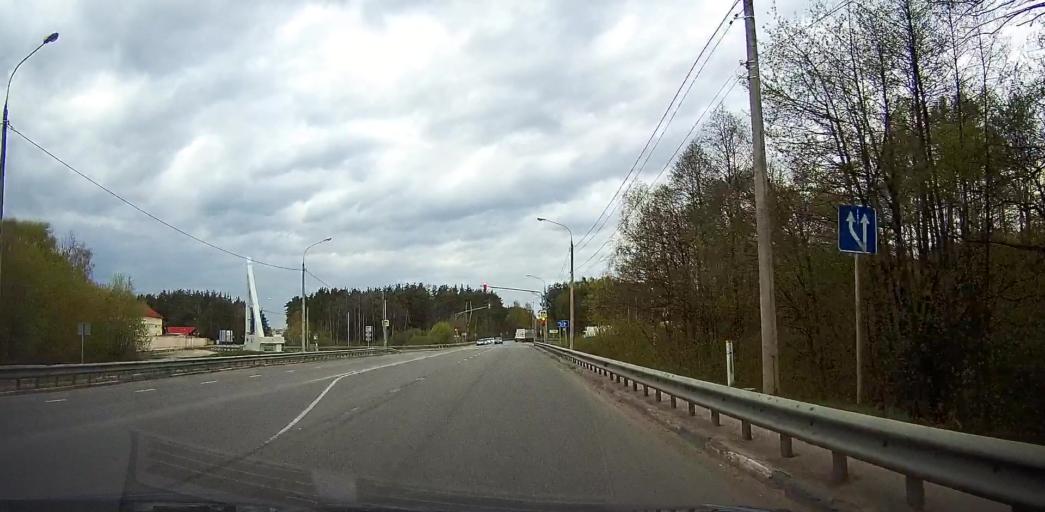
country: RU
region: Moskovskaya
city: Pavlovskiy Posad
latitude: 55.7997
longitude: 38.6523
